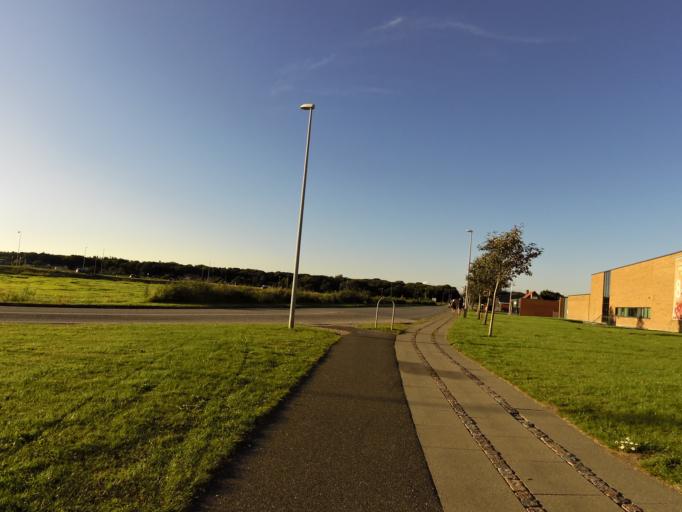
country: DK
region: South Denmark
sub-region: Esbjerg Kommune
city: Ribe
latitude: 55.3338
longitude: 8.7692
